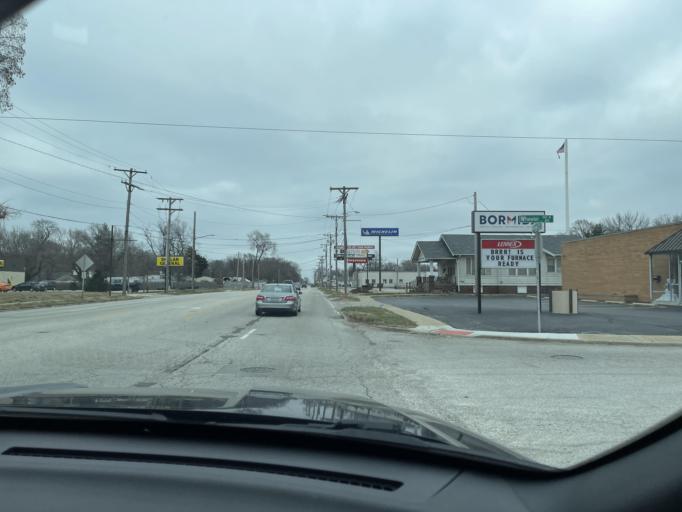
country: US
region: Illinois
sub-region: Sangamon County
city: Grandview
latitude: 39.8018
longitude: -89.6253
